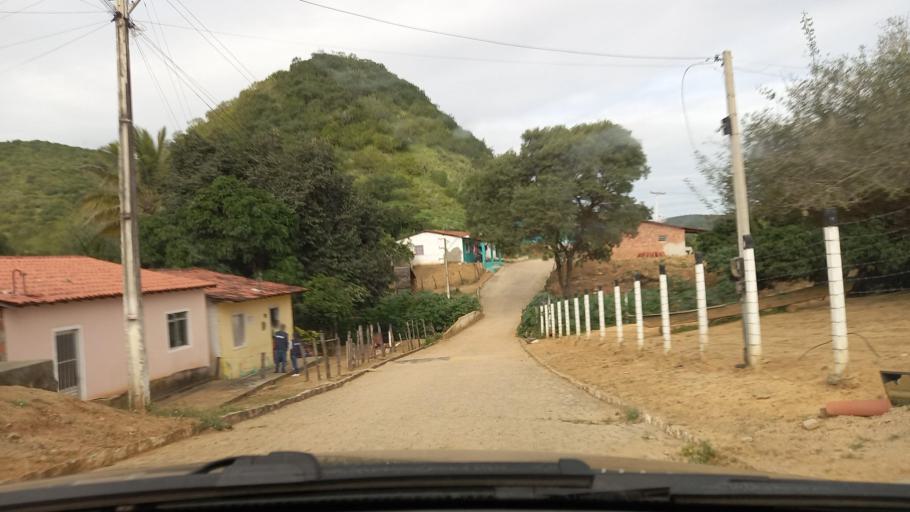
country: BR
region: Sergipe
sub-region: Caninde De Sao Francisco
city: Caninde de Sao Francisco
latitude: -9.6223
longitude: -37.7462
